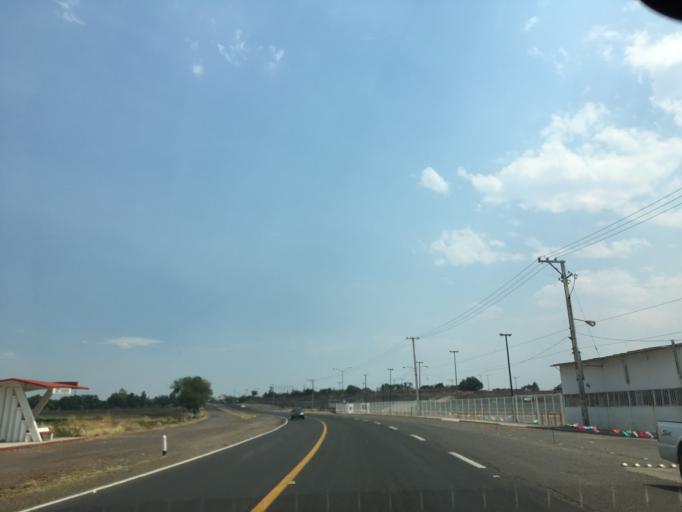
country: MX
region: Michoacan
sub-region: Cuitzeo
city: Cuamio
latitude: 20.0701
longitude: -101.1554
